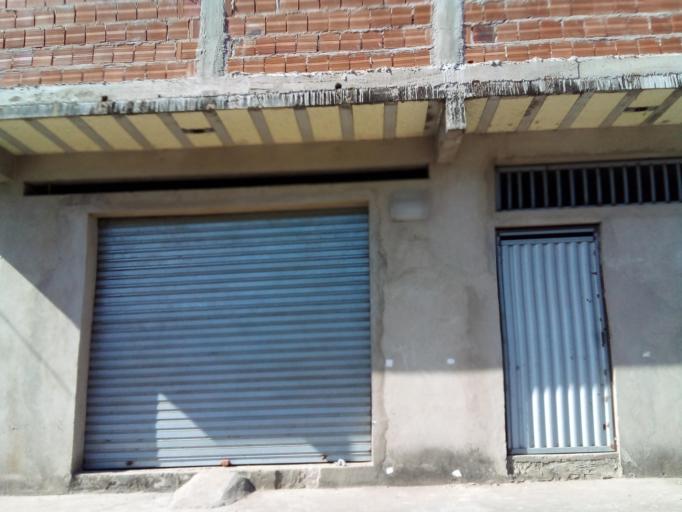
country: BR
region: Espirito Santo
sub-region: Vitoria
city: Vitoria
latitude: -20.2983
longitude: -40.3738
